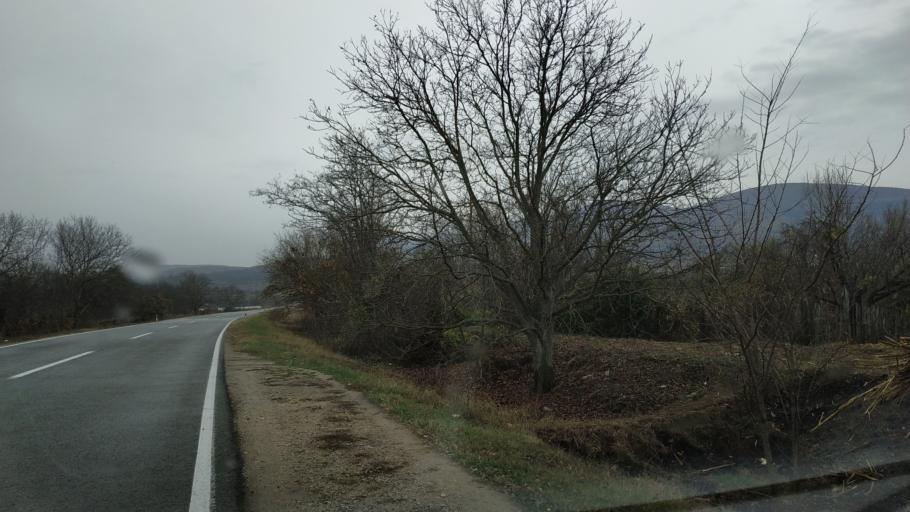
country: RS
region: Central Serbia
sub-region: Pirotski Okrug
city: Bela Palanka
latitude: 43.2292
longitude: 22.3260
